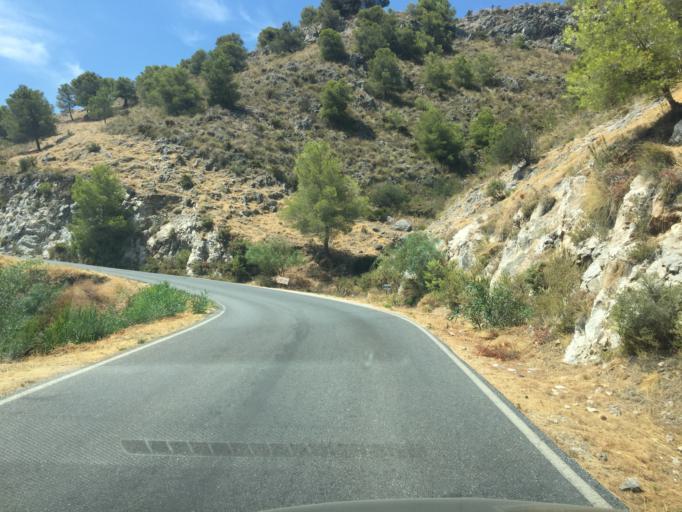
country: ES
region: Andalusia
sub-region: Provincia de Malaga
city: Frigiliana
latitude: 36.8003
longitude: -3.9064
